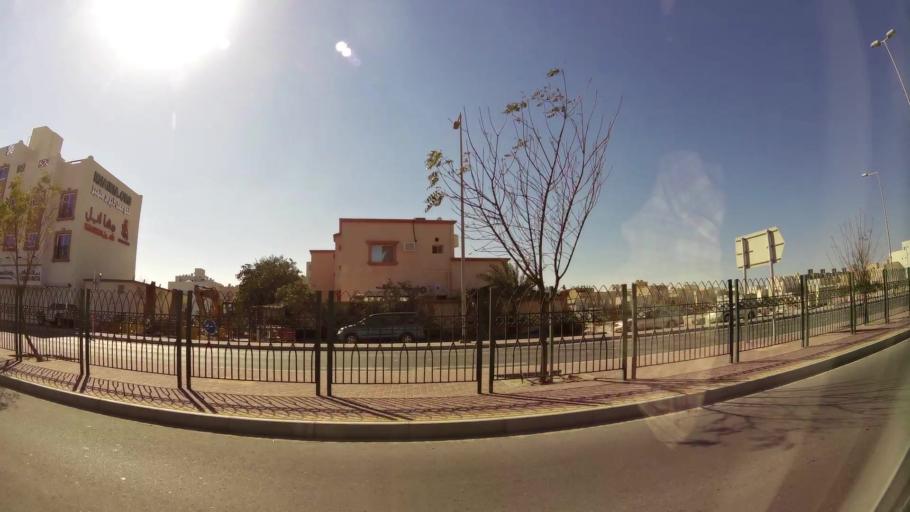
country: BH
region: Muharraq
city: Al Hadd
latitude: 26.2435
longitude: 50.6519
